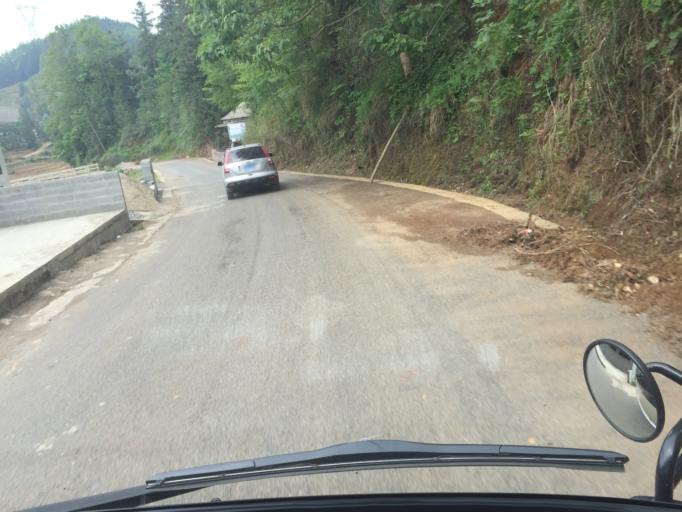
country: CN
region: Guangxi Zhuangzu Zizhiqu
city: Xinzhou
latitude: 25.6811
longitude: 105.2334
